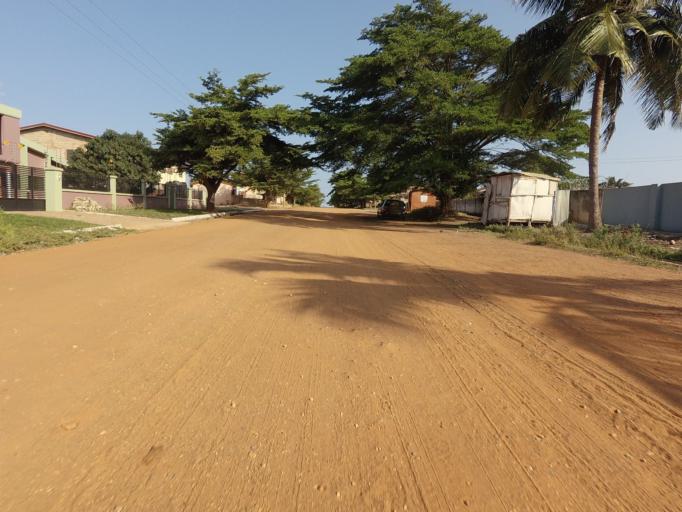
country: GH
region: Greater Accra
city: Nungua
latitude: 5.6390
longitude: -0.0861
